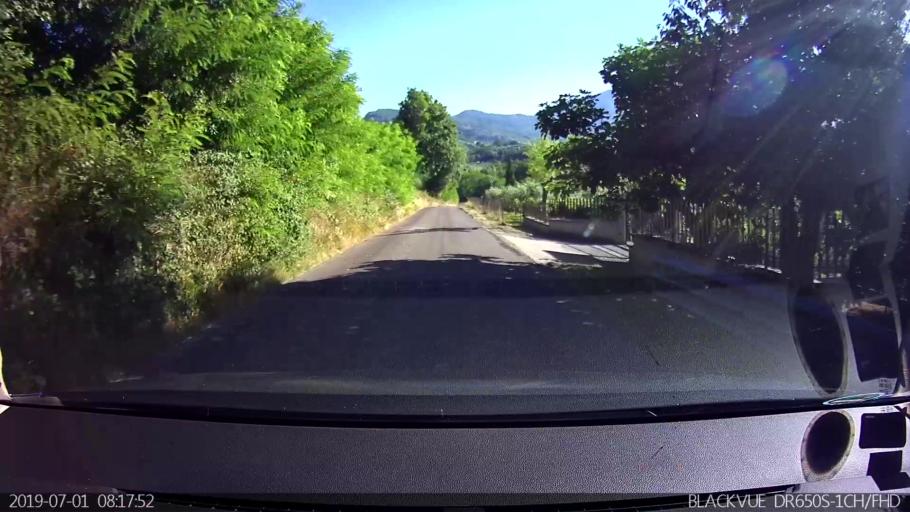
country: IT
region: Latium
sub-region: Provincia di Frosinone
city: Veroli
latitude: 41.7096
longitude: 13.4402
